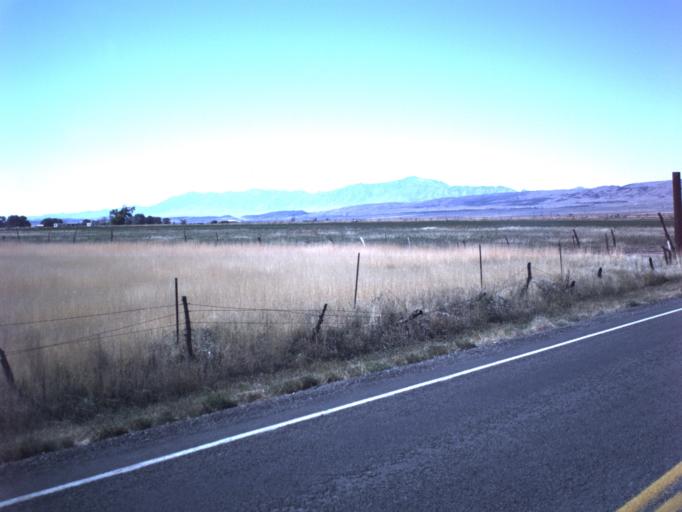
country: US
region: Utah
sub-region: Juab County
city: Nephi
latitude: 39.5584
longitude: -111.8749
